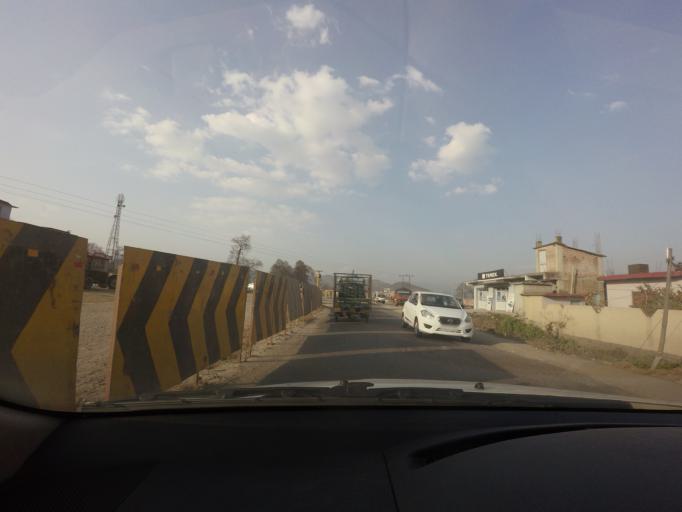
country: IN
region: Himachal Pradesh
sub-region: Mandi
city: Sundarnagar
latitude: 31.5957
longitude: 76.9243
